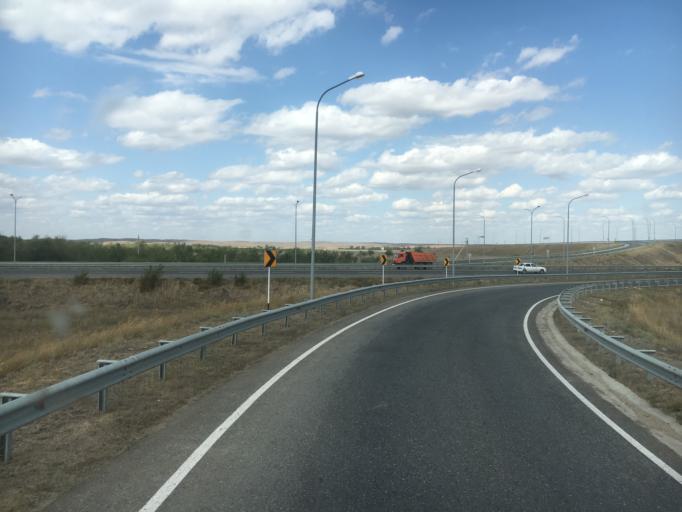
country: KZ
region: Aqtoebe
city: Aqtobe
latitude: 50.2932
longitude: 57.4344
